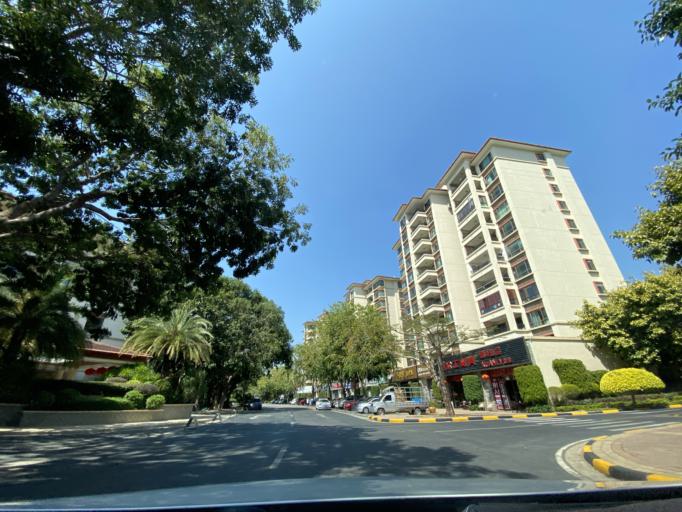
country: CN
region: Hainan
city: Yingzhou
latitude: 18.4073
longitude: 109.8500
